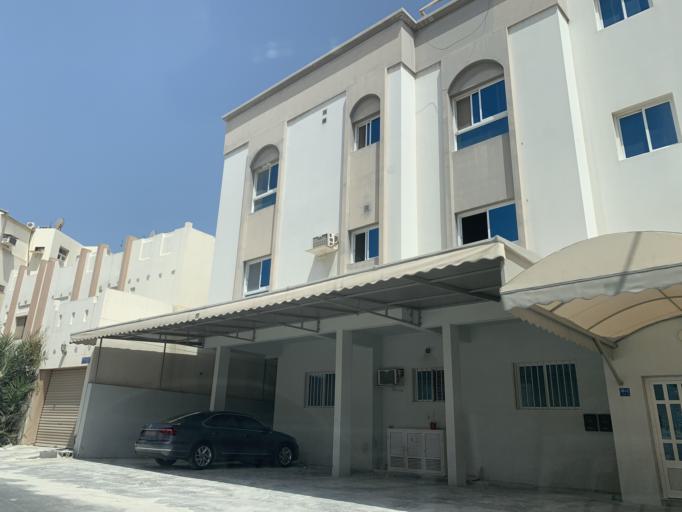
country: BH
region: Muharraq
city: Al Muharraq
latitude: 26.2799
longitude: 50.6083
